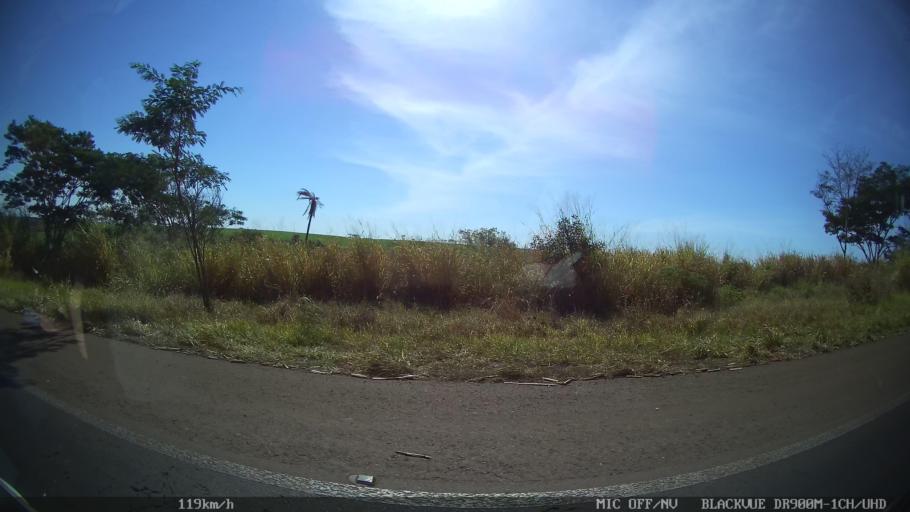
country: BR
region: Sao Paulo
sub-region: Olimpia
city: Olimpia
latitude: -20.6274
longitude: -48.7933
